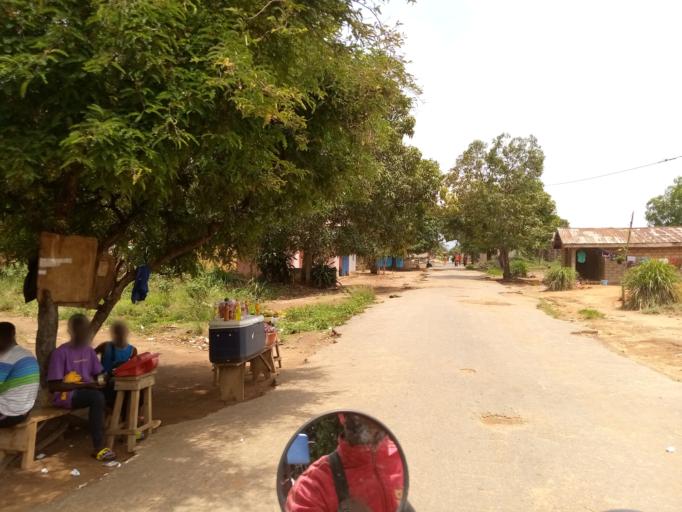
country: SL
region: Western Area
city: Waterloo
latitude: 8.3342
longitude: -13.0190
